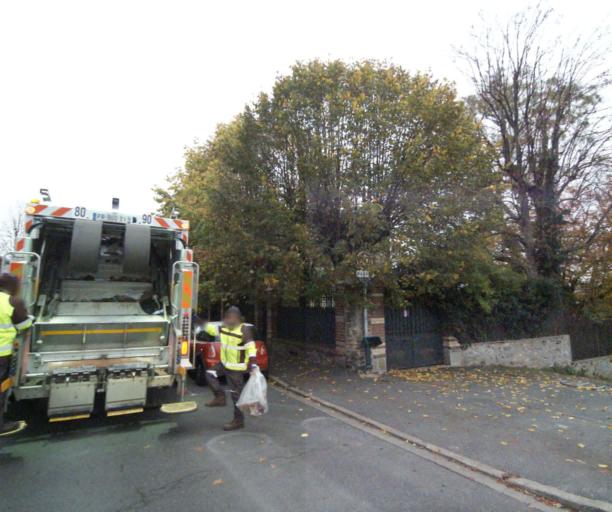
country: FR
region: Ile-de-France
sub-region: Departement des Yvelines
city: Triel-sur-Seine
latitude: 48.9803
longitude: 2.0059
